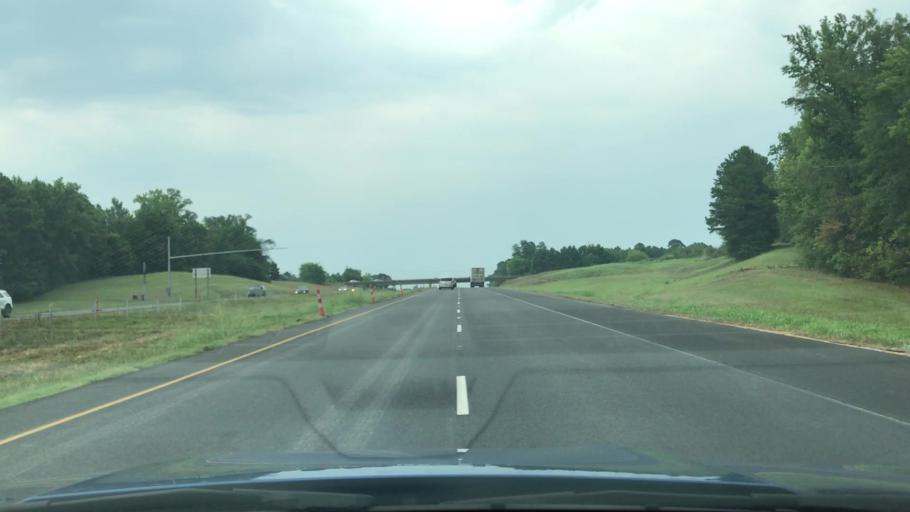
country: US
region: Louisiana
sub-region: Caddo Parish
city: Greenwood
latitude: 32.4516
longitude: -94.0156
